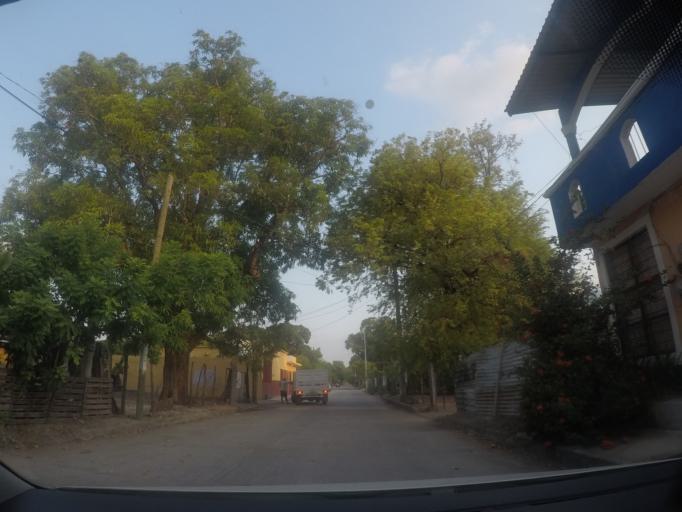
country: MX
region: Oaxaca
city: San Jeronimo Ixtepec
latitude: 16.5861
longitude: -95.2102
